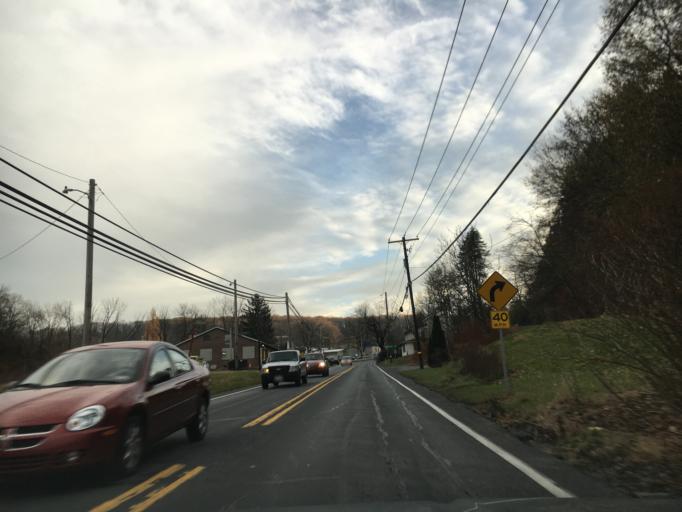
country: US
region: Pennsylvania
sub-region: Lehigh County
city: Slatington
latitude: 40.7261
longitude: -75.6172
